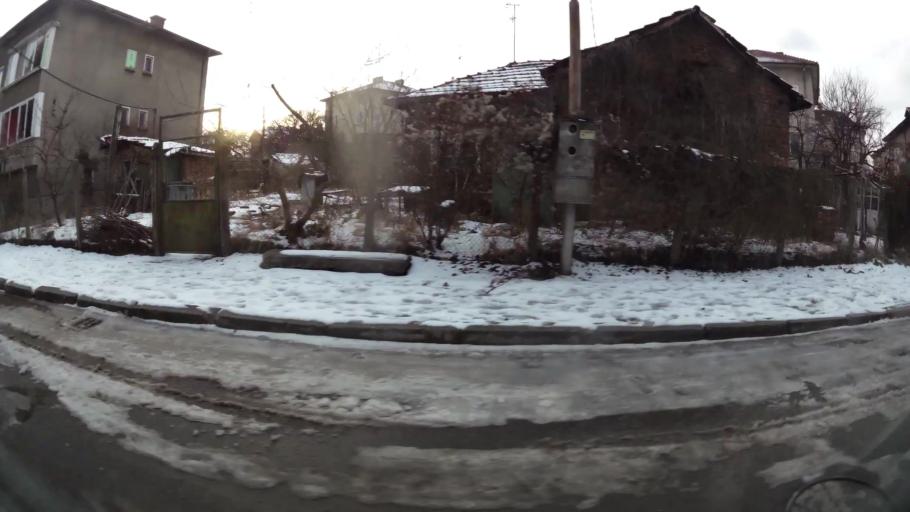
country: BG
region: Sofia-Capital
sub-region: Stolichna Obshtina
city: Sofia
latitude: 42.7209
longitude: 23.3458
